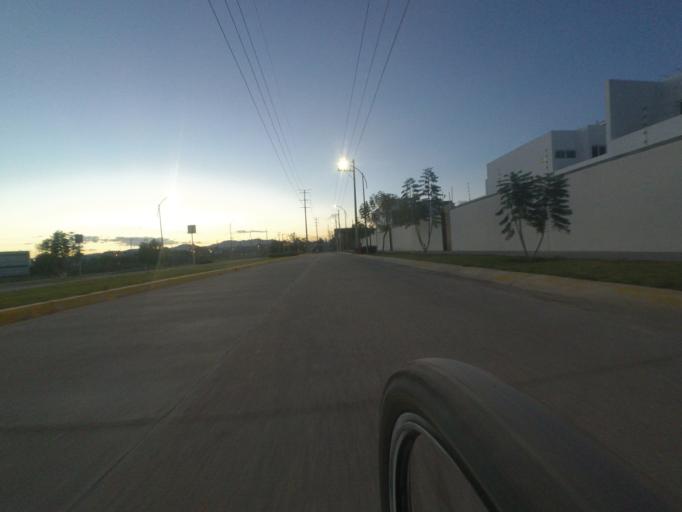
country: MX
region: Aguascalientes
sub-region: Aguascalientes
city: La Loma de los Negritos
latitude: 21.8533
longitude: -102.3316
